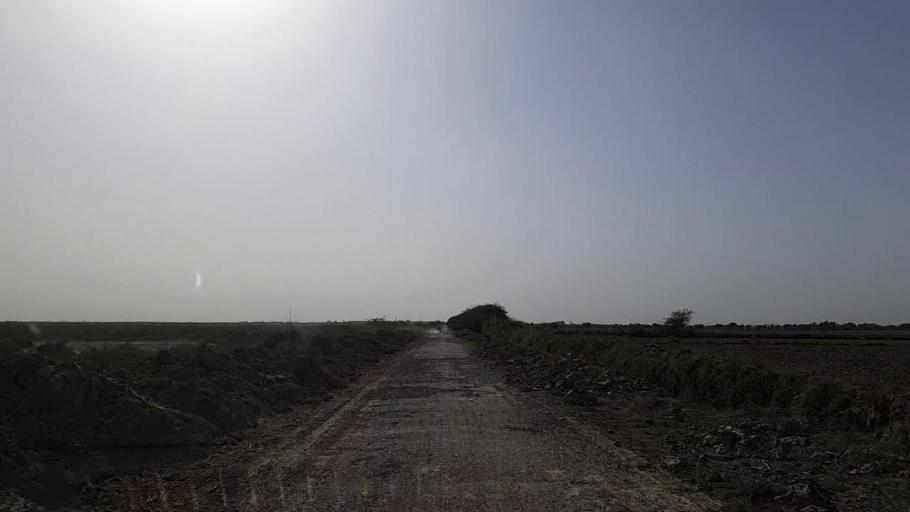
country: PK
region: Sindh
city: Jati
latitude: 24.2819
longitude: 68.2402
